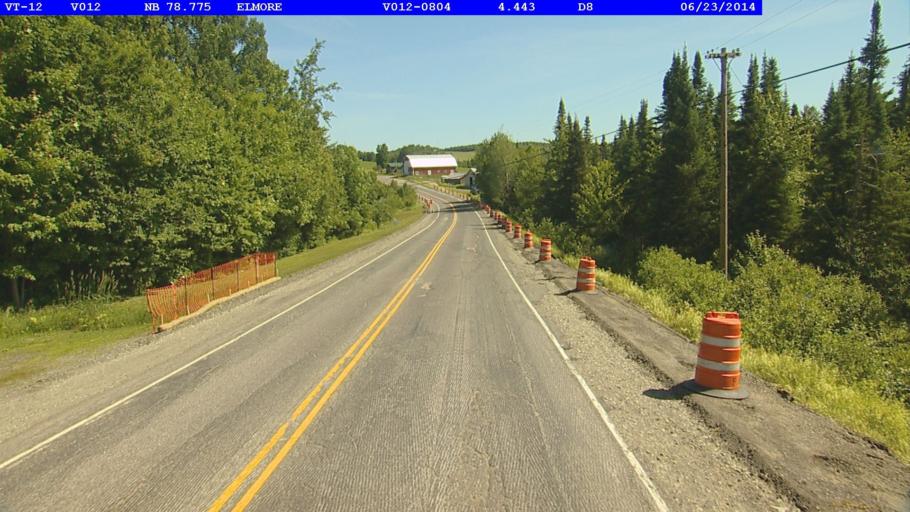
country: US
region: Vermont
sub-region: Lamoille County
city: Morrisville
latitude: 44.5090
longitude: -72.5135
